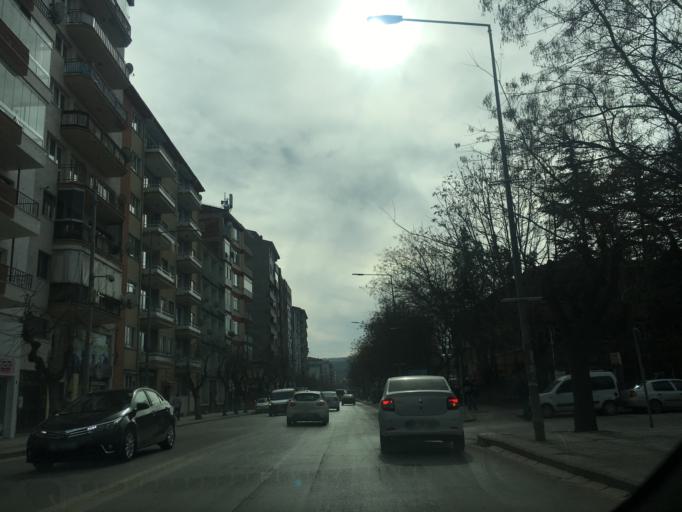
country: TR
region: Eskisehir
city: Eskisehir
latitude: 39.7725
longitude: 30.5140
